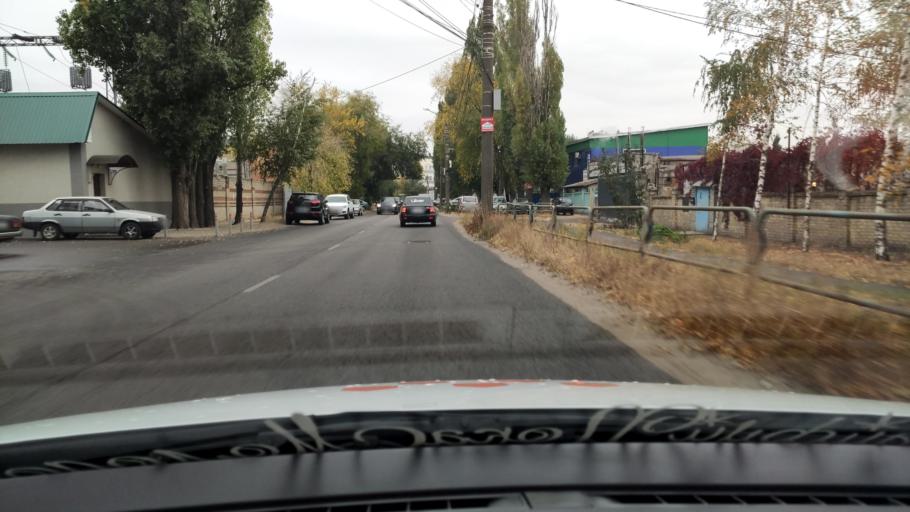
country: RU
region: Voronezj
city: Voronezh
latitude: 51.6837
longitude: 39.1702
